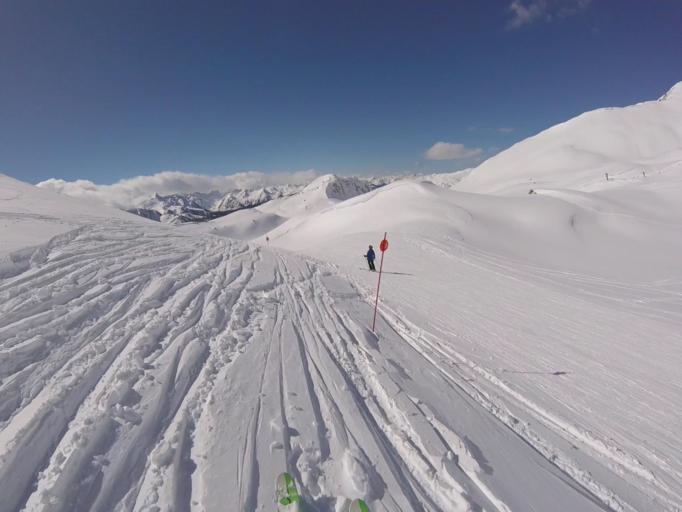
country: ES
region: Catalonia
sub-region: Provincia de Lleida
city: Espot
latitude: 42.6761
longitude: 0.9907
